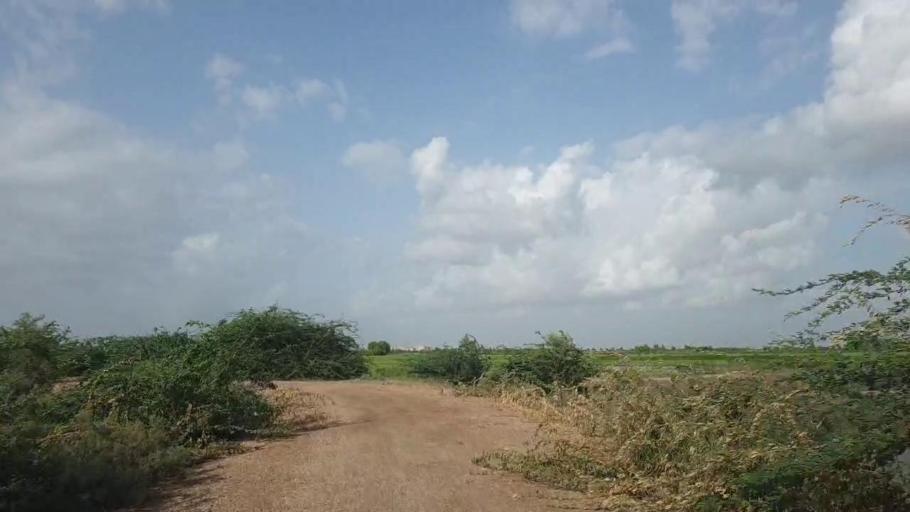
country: PK
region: Sindh
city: Kadhan
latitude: 24.6307
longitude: 69.0874
